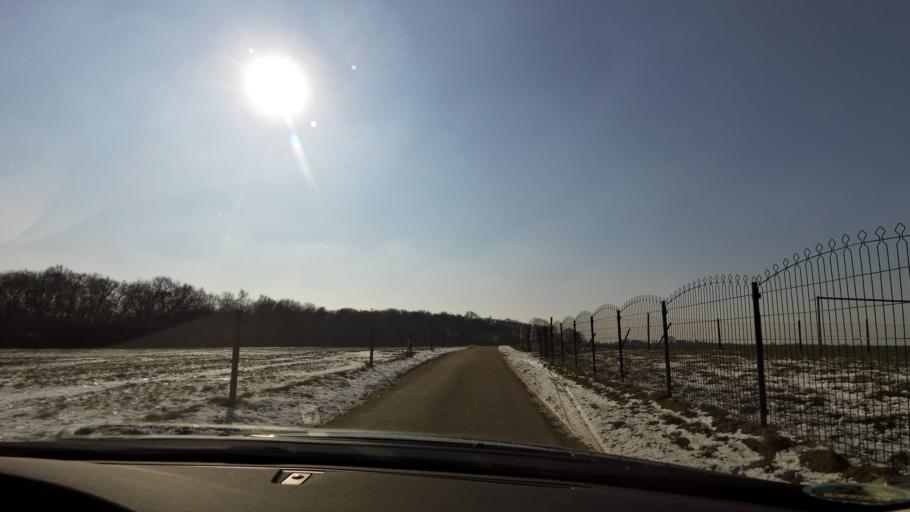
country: NL
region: Limburg
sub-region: Valkenburg aan de Geul
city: Schin op Geul
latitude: 50.8307
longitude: 5.8696
